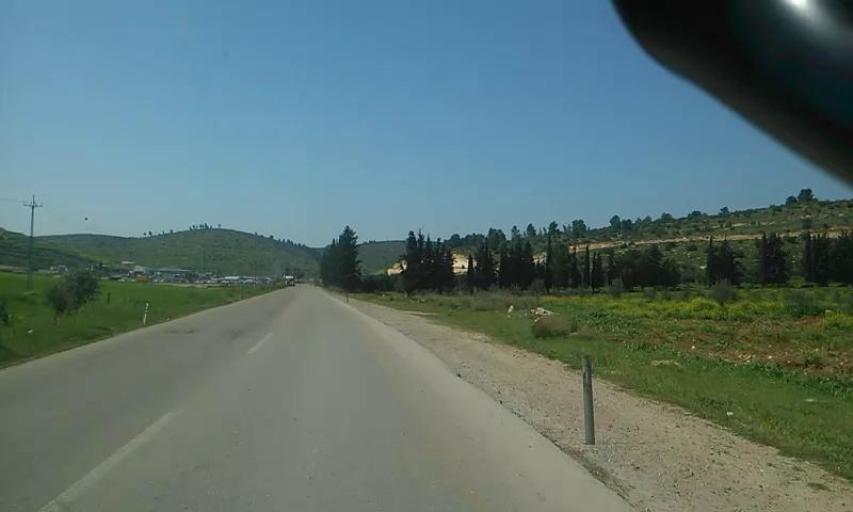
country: PS
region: West Bank
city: Idhna
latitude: 31.5894
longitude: 34.9687
